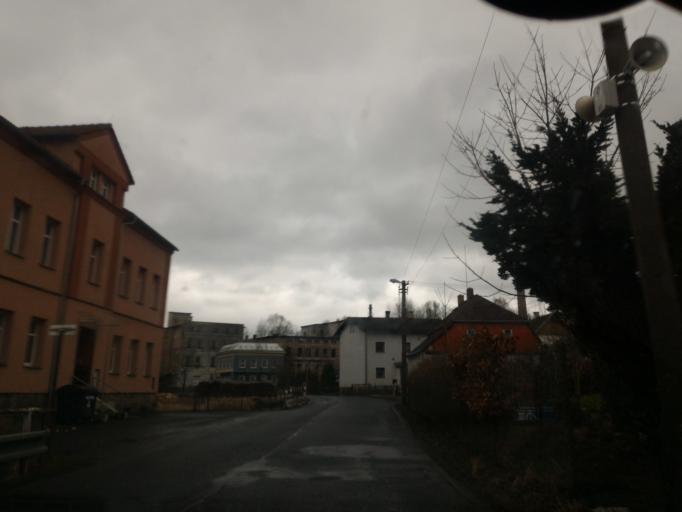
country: CZ
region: Ustecky
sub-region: Okres Decin
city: Krasna Lipa
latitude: 50.9159
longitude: 14.4980
